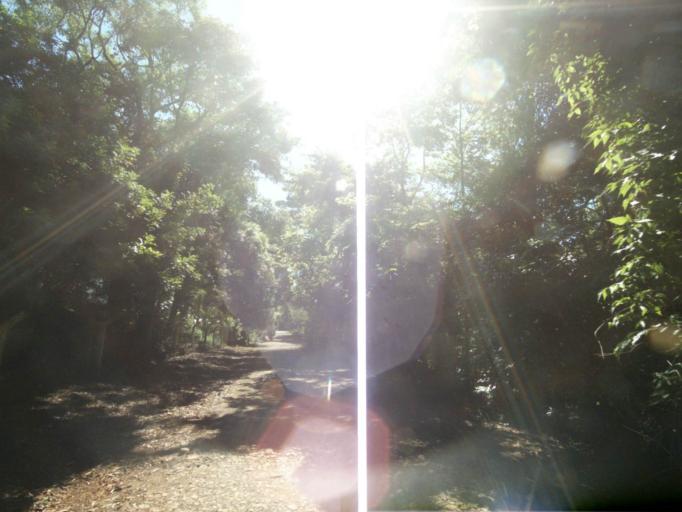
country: BR
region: Parana
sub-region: Ampere
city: Ampere
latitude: -26.1683
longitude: -53.3624
